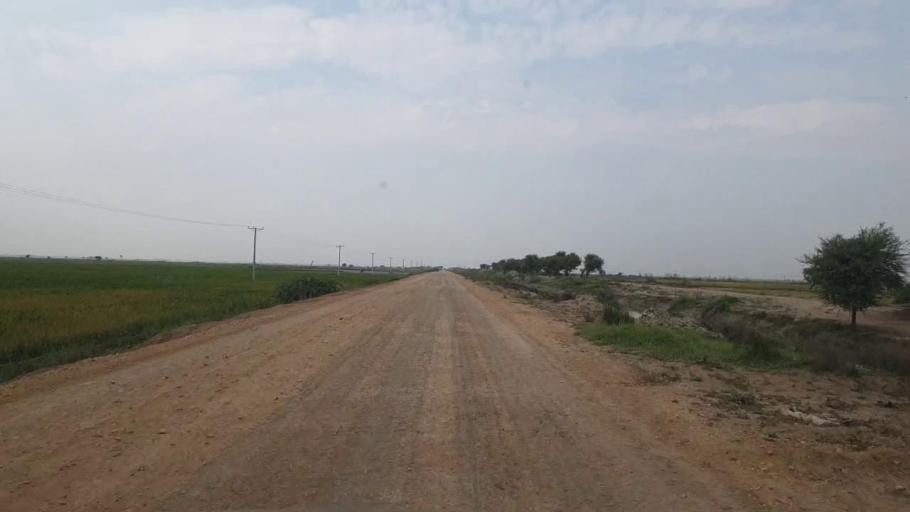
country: PK
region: Sindh
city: Kario
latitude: 24.6119
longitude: 68.5912
